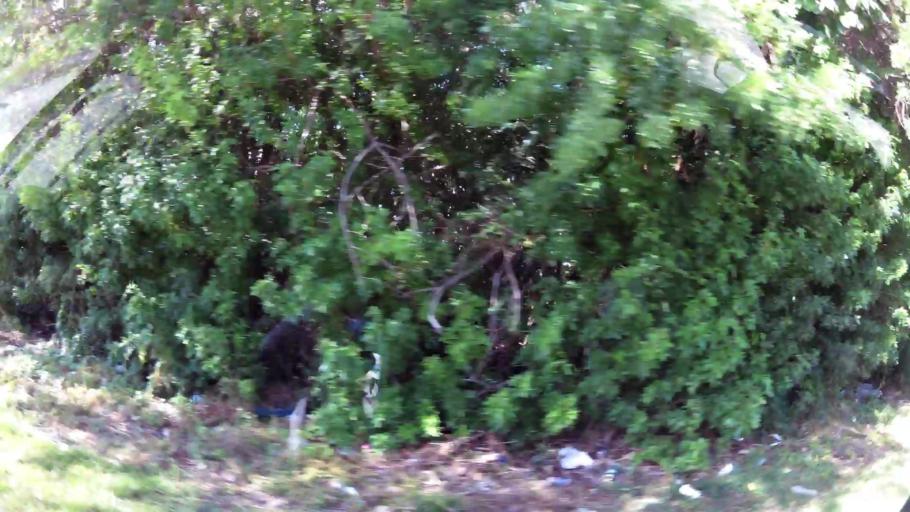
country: BS
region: Freeport
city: Freeport
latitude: 26.5181
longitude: -78.6920
